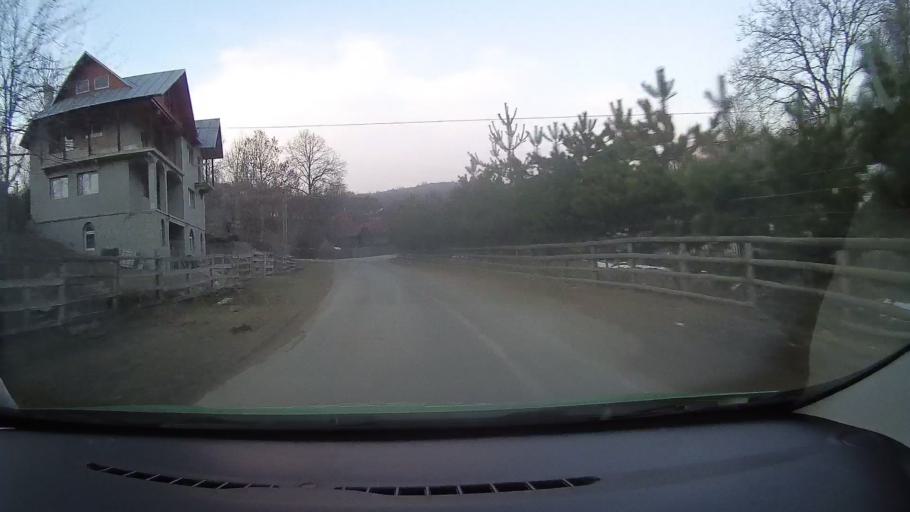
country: RO
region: Prahova
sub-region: Comuna Secaria
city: Secaria
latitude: 45.2757
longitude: 25.6872
